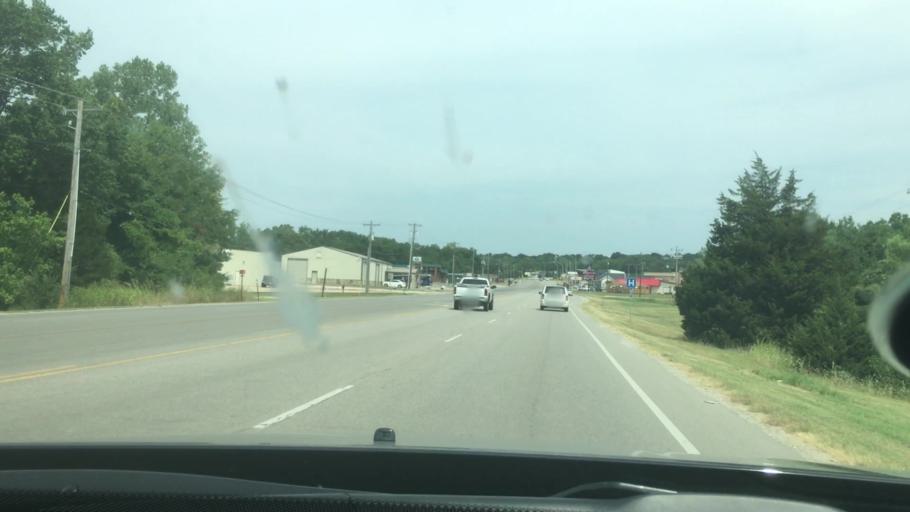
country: US
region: Oklahoma
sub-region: Pontotoc County
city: Ada
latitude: 34.7573
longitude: -96.6602
